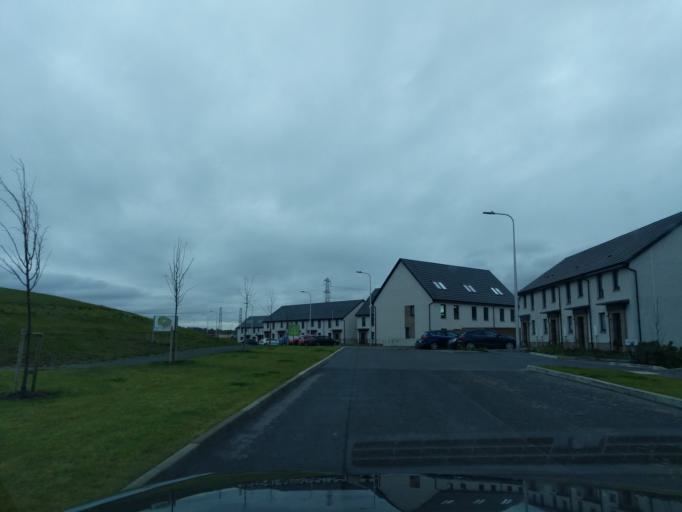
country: GB
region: Scotland
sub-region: Midlothian
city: Loanhead
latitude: 55.8977
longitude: -3.1667
